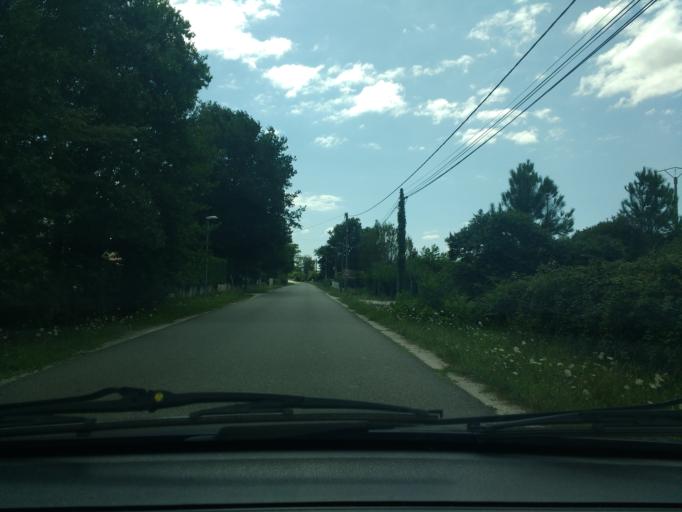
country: FR
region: Aquitaine
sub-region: Departement de la Gironde
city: Salles
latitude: 44.5625
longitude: -0.8470
